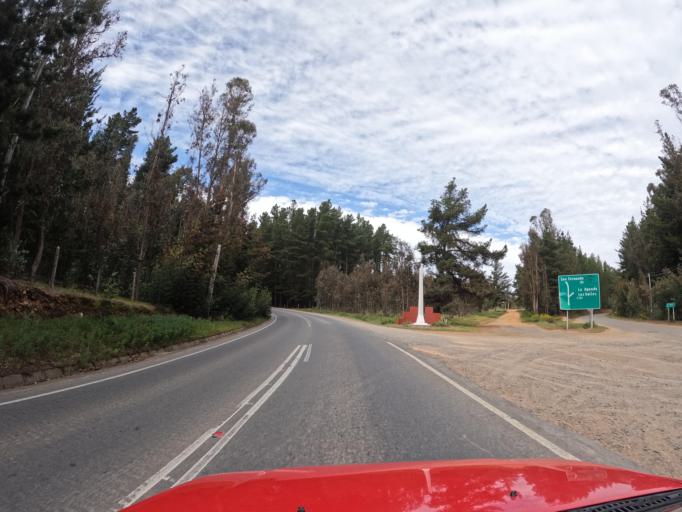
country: CL
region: O'Higgins
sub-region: Provincia de Colchagua
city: Santa Cruz
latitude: -34.3569
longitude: -71.8683
